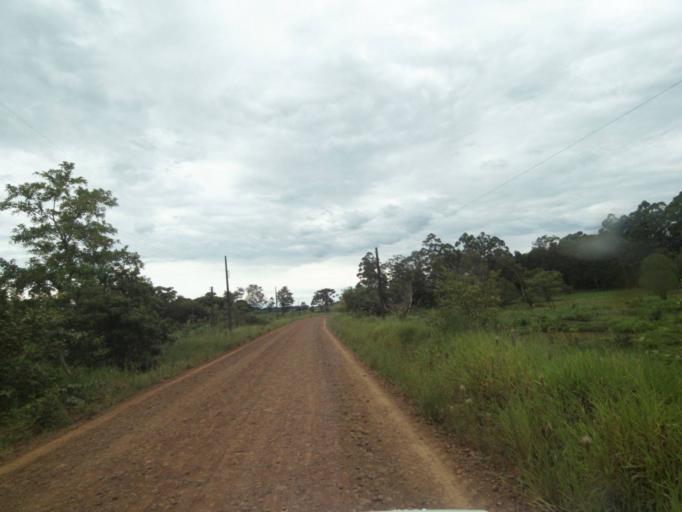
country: BR
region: Parana
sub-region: Guaraniacu
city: Guaraniacu
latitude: -24.9095
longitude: -52.9356
